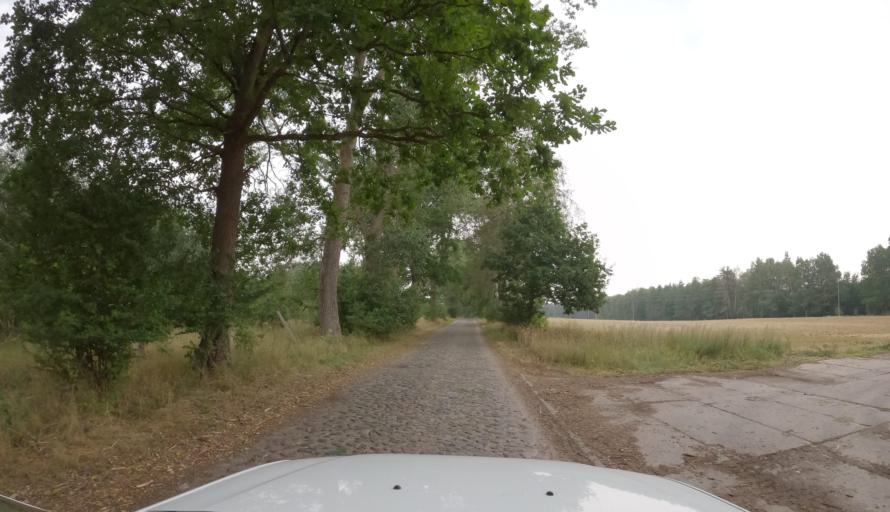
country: PL
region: West Pomeranian Voivodeship
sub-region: Powiat kolobrzeski
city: Ryman
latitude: 53.8517
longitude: 15.5875
